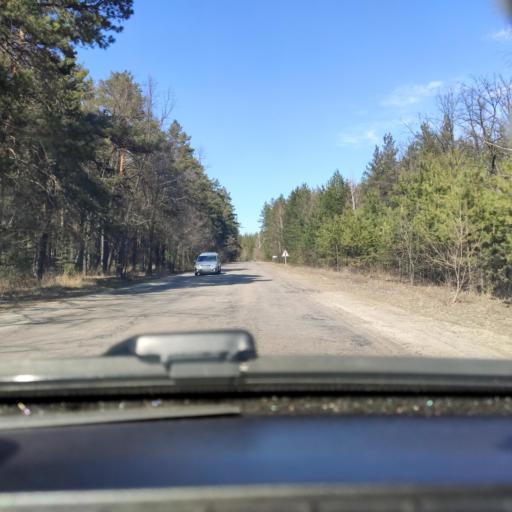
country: RU
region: Voronezj
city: Somovo
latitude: 51.7244
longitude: 39.3670
